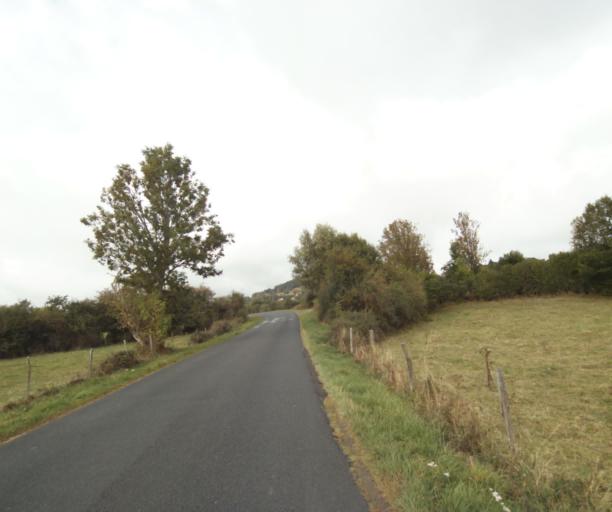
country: FR
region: Auvergne
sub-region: Departement du Puy-de-Dome
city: Saint-Genes-Champanelle
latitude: 45.7101
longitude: 3.0002
